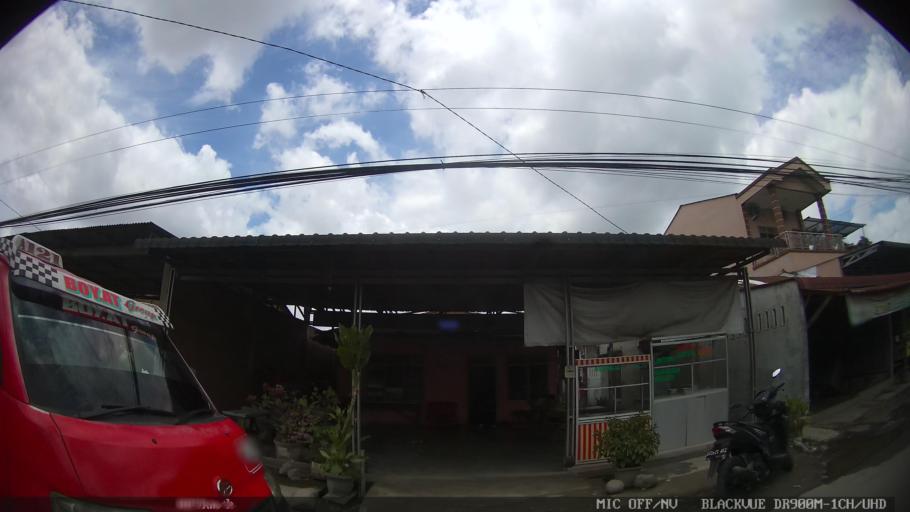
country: ID
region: North Sumatra
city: Medan
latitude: 3.6186
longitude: 98.7293
